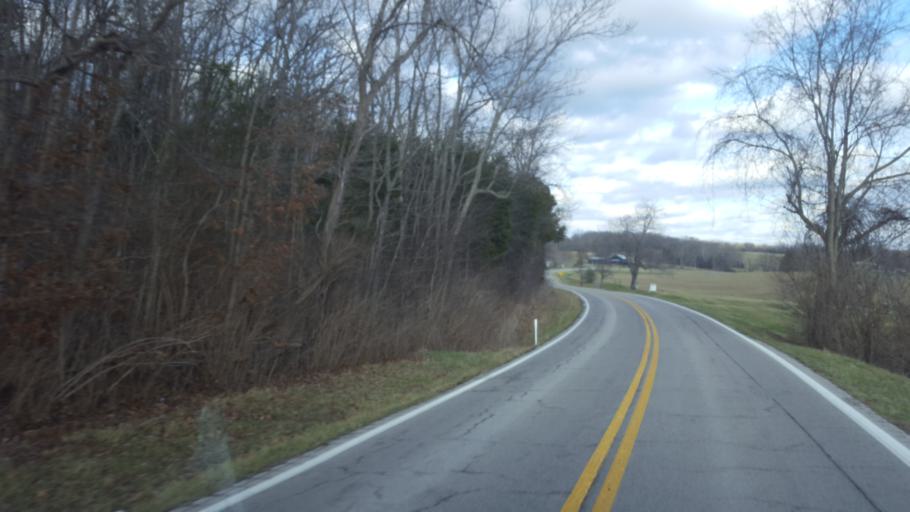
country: US
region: Kentucky
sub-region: Robertson County
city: Mount Olivet
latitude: 38.4609
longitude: -84.0335
